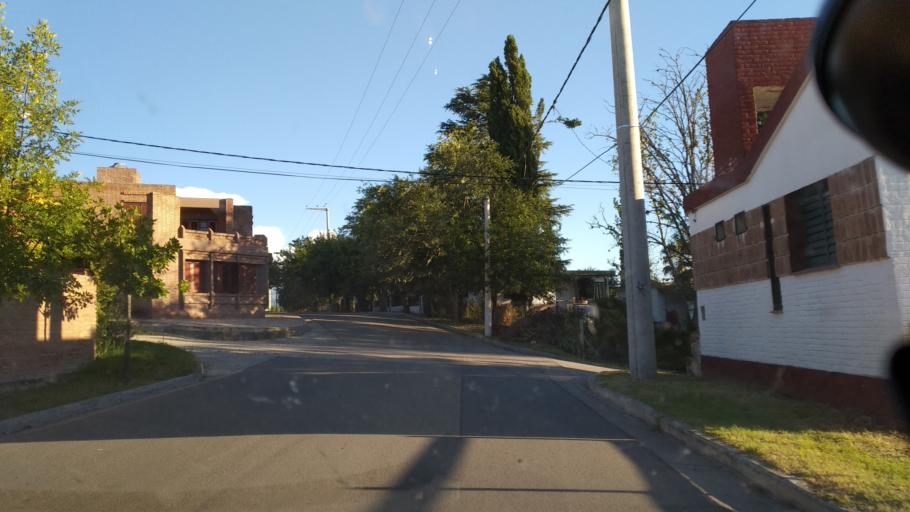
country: AR
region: Cordoba
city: Mina Clavero
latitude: -31.7191
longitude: -65.0026
